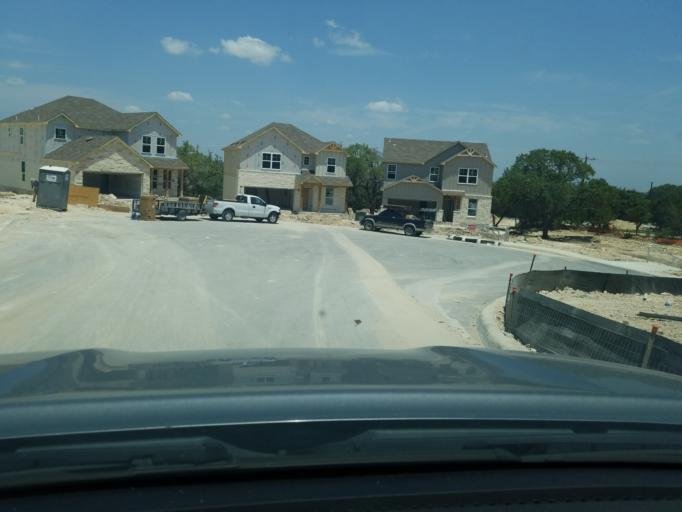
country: US
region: Texas
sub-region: Bexar County
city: Timberwood Park
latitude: 29.7072
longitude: -98.4986
